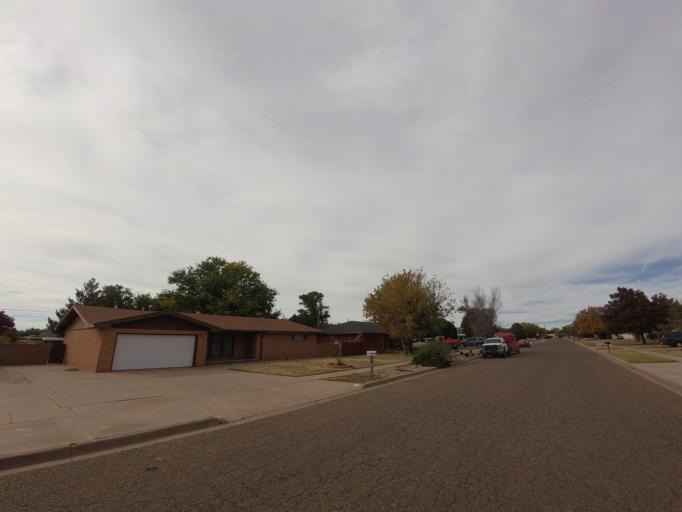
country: US
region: New Mexico
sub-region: Curry County
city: Clovis
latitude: 34.4222
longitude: -103.2129
